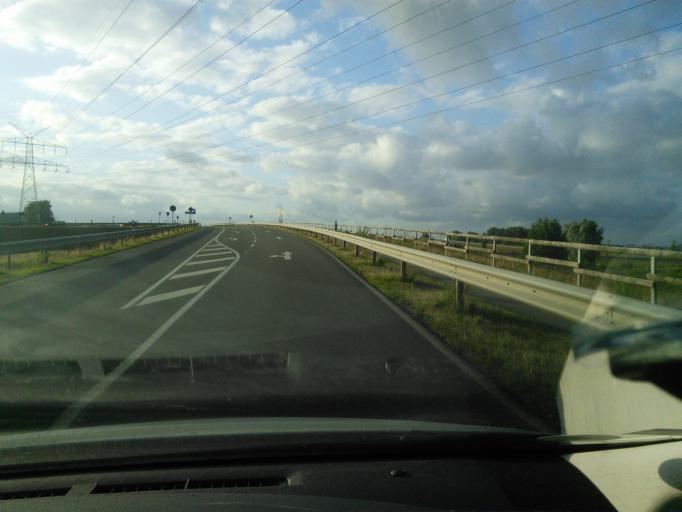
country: DE
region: Lower Saxony
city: Agathenburg
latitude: 53.5777
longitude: 9.5197
